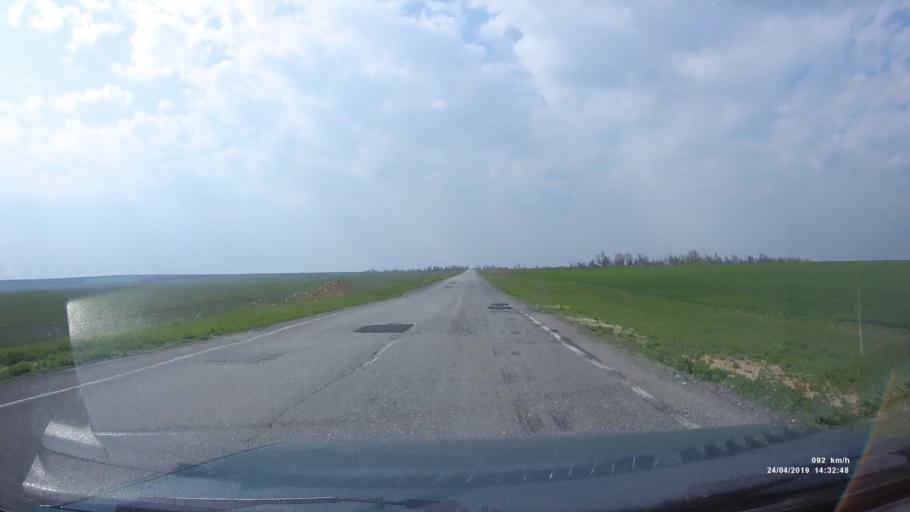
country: RU
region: Kalmykiya
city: Arshan'
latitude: 46.3679
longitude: 43.9632
